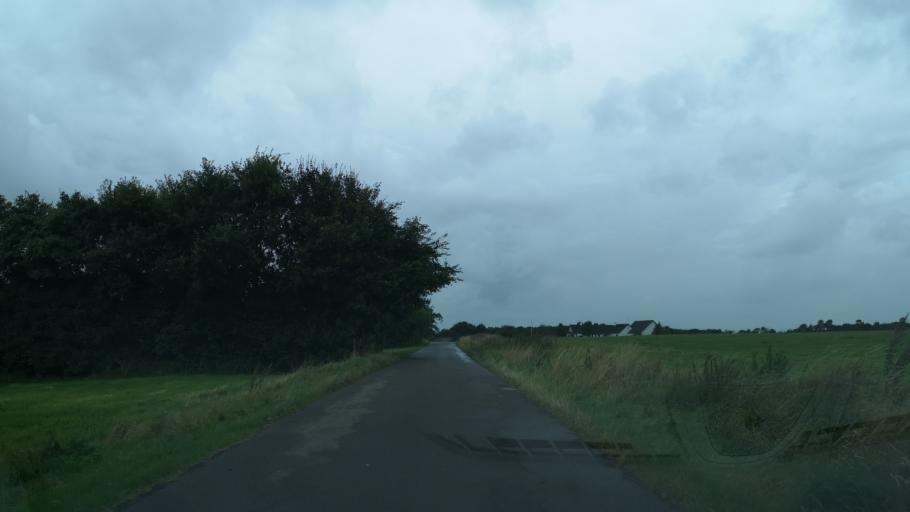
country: DK
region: Central Jutland
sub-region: Ringkobing-Skjern Kommune
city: Skjern
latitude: 55.9718
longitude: 8.5489
